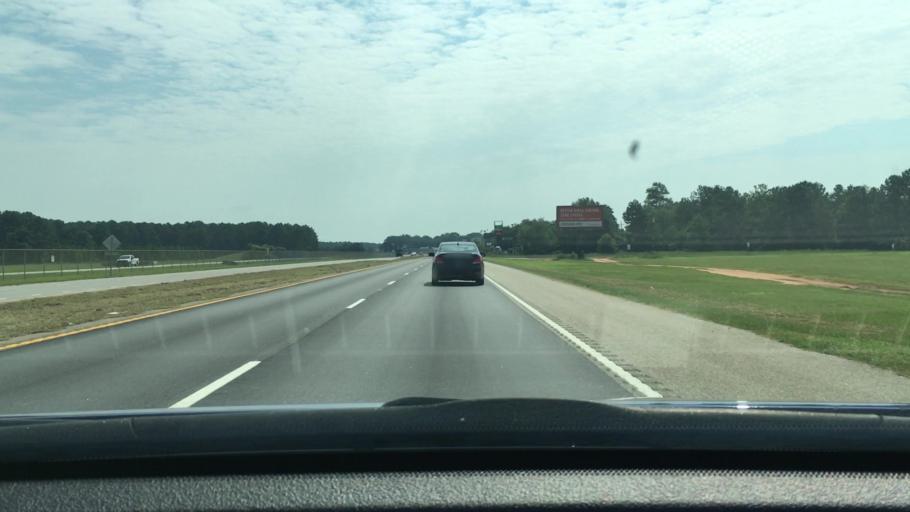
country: US
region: South Carolina
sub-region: Sumter County
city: Cherryvale
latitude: 33.9601
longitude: -80.4737
